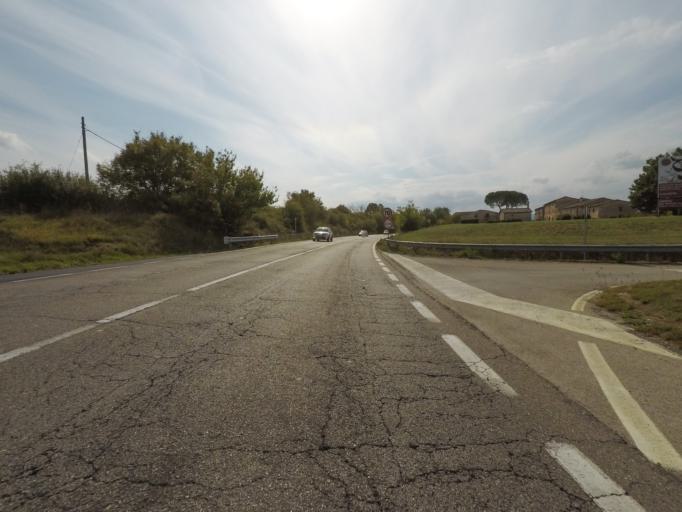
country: IT
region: Tuscany
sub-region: Provincia di Siena
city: Rosia
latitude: 43.2095
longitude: 11.2791
